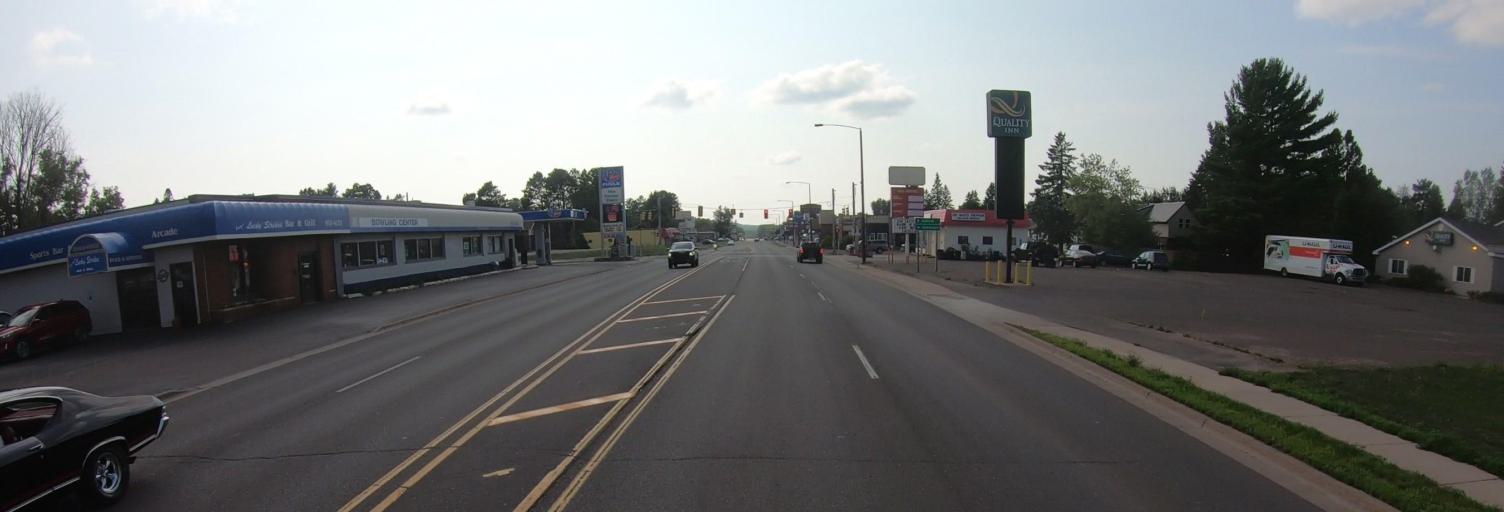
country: US
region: Michigan
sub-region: Gogebic County
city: Ironwood
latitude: 46.4632
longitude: -90.1679
